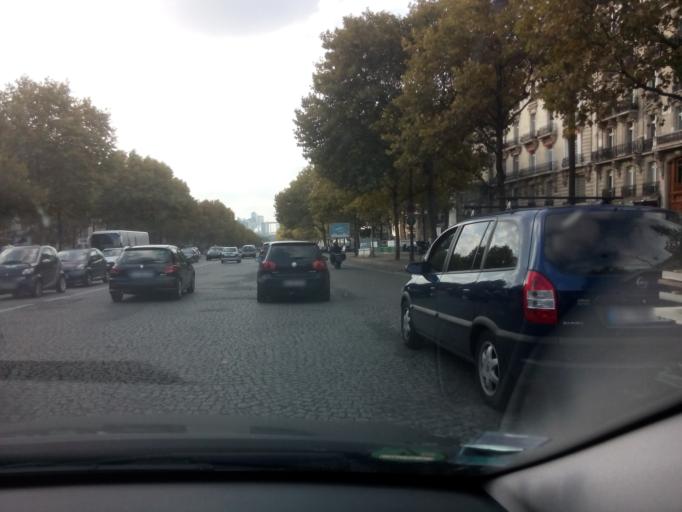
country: FR
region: Ile-de-France
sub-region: Departement des Hauts-de-Seine
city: Levallois-Perret
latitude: 48.8745
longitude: 2.2927
